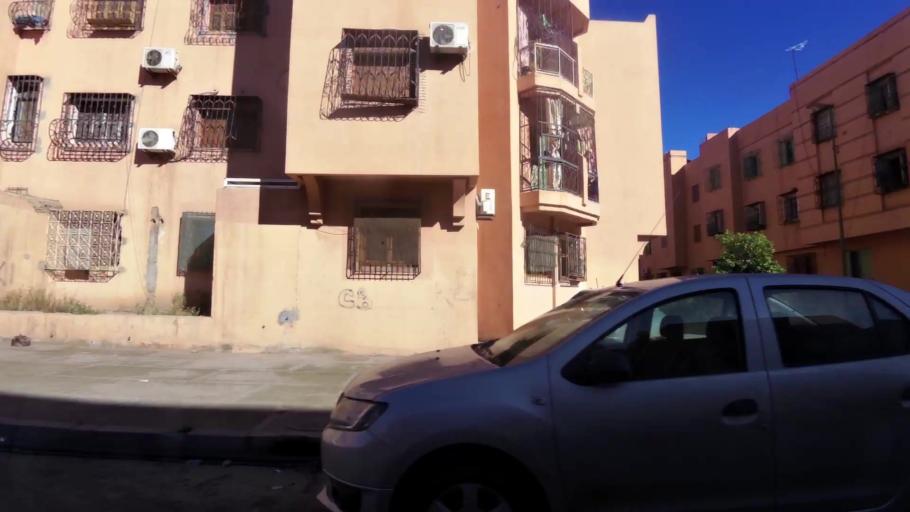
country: MA
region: Marrakech-Tensift-Al Haouz
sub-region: Marrakech
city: Marrakesh
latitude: 31.5946
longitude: -8.0271
